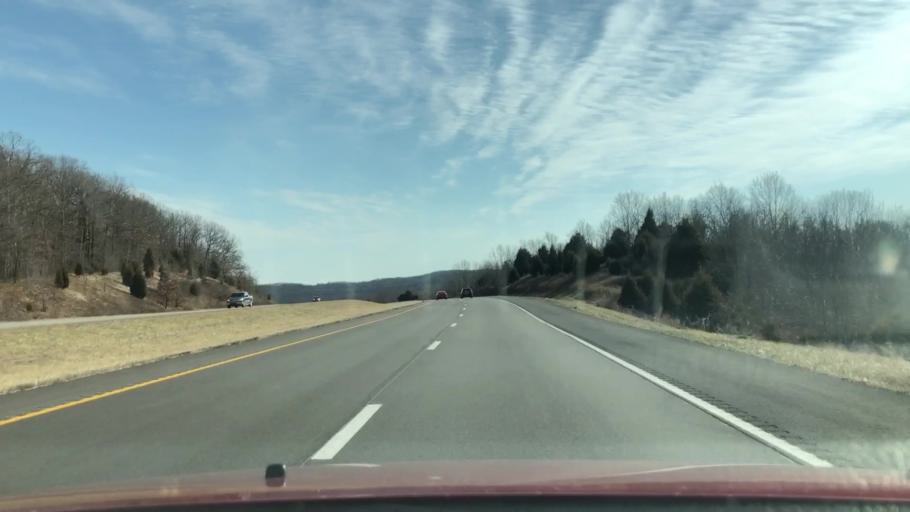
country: US
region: Missouri
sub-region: Wright County
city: Mansfield
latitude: 37.1140
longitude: -92.6720
